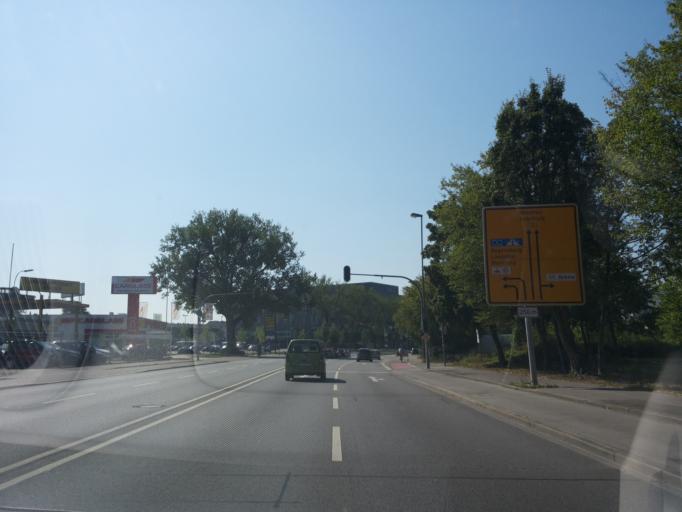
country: DE
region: Bavaria
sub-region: Upper Bavaria
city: Ingolstadt
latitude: 48.7610
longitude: 11.4402
